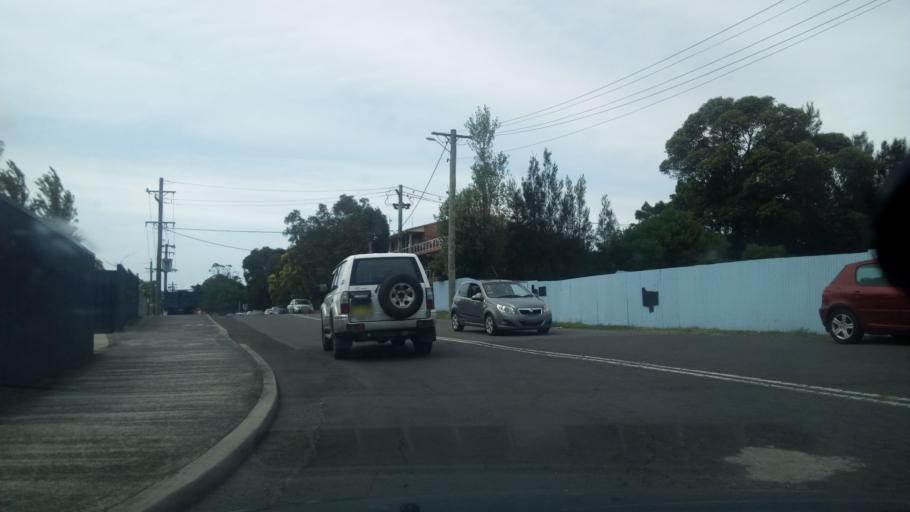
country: AU
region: New South Wales
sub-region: Wollongong
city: Gwynneville
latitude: -34.4108
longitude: 150.8940
